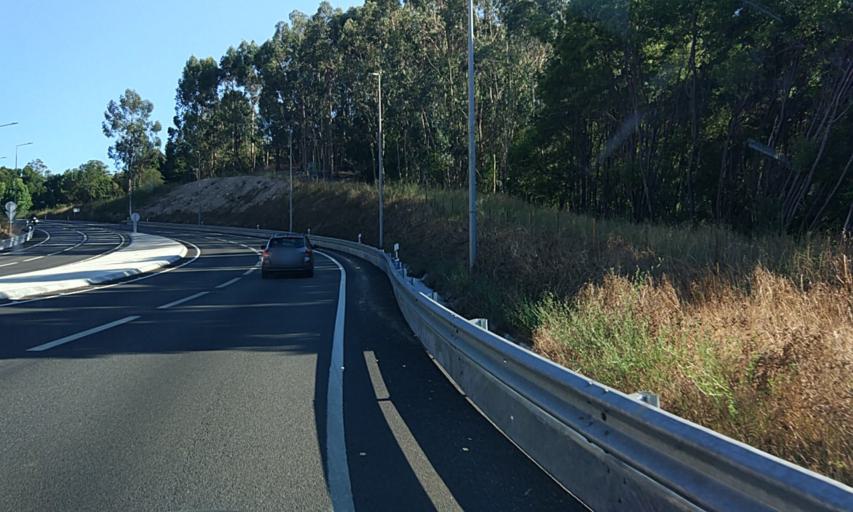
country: PT
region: Porto
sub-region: Santo Tirso
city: Santo Tirso
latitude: 41.3363
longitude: -8.4705
